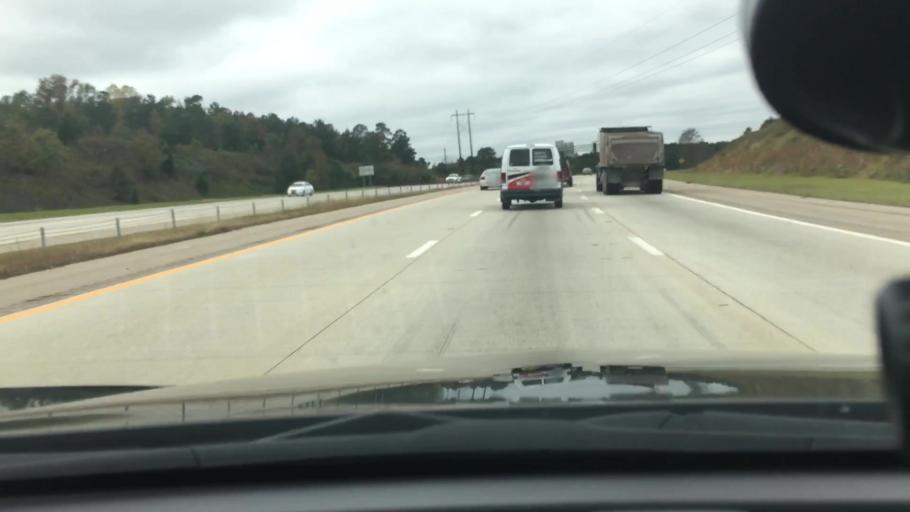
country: US
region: North Carolina
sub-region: Wake County
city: Knightdale
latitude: 35.7687
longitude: -78.5241
